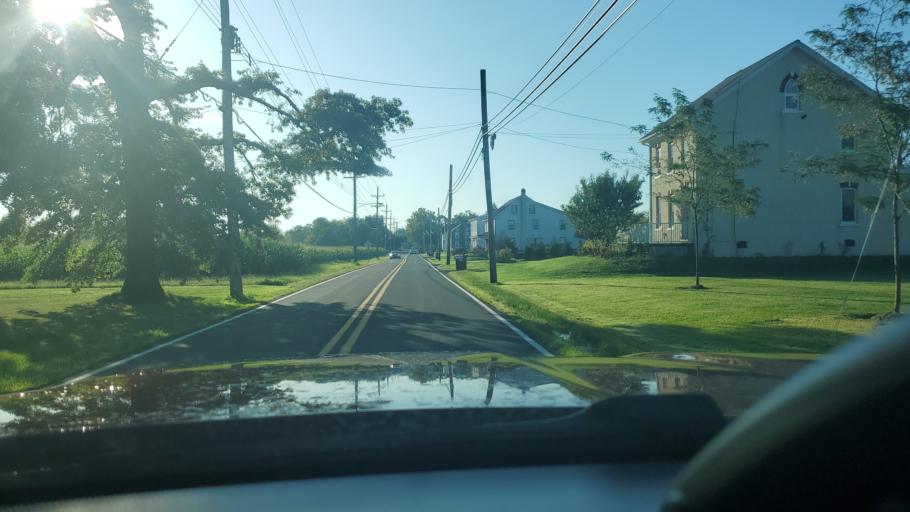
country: US
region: Pennsylvania
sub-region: Montgomery County
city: Woxall
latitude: 40.2957
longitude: -75.4366
